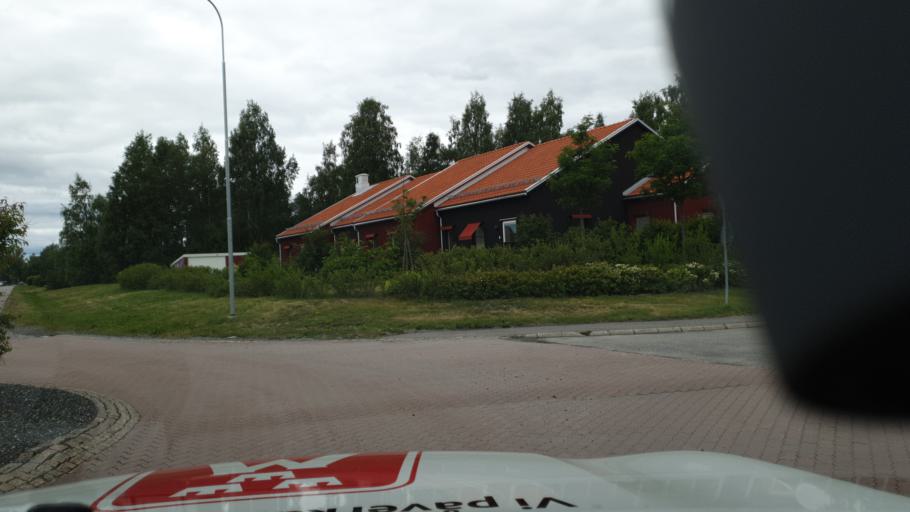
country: SE
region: Vaesterbotten
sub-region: Skelleftea Kommun
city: Skelleftea
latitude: 64.7523
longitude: 20.9307
